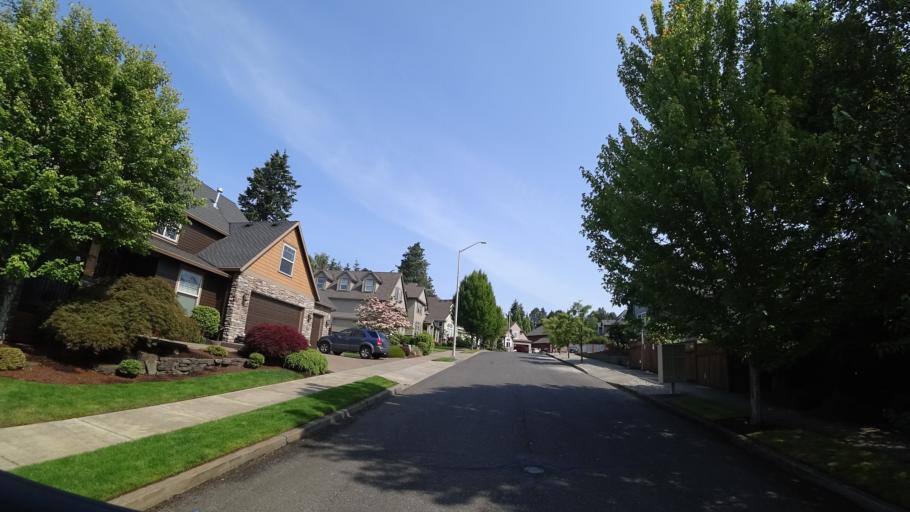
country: US
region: Oregon
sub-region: Clackamas County
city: Happy Valley
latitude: 45.4600
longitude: -122.5168
